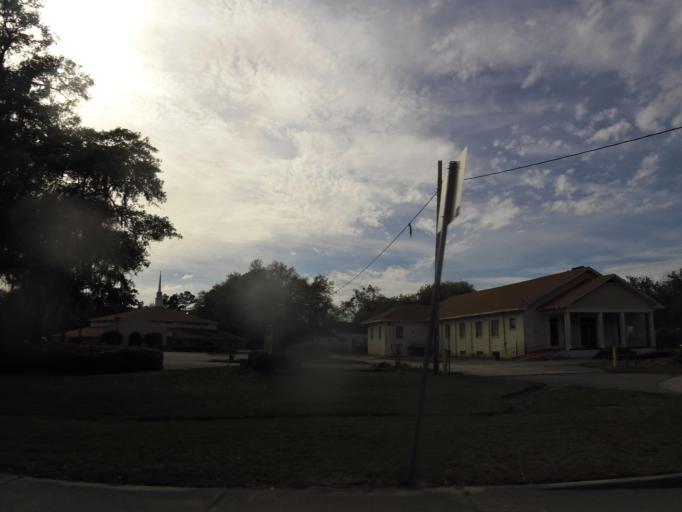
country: US
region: Florida
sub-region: Clay County
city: Bellair-Meadowbrook Terrace
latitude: 30.2743
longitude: -81.7710
